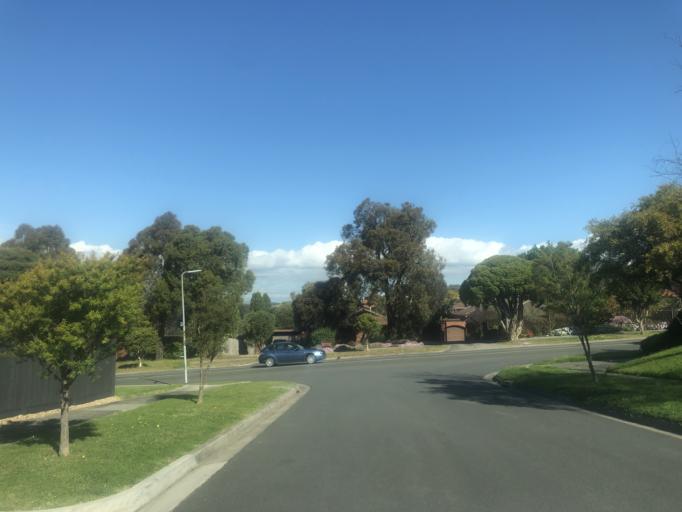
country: AU
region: Victoria
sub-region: Monash
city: Mulgrave
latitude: -37.9094
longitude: 145.1971
